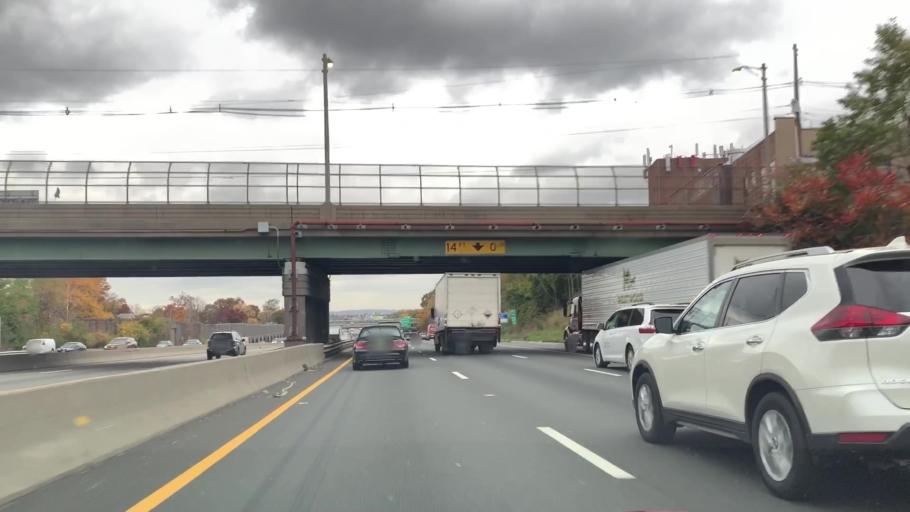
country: US
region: New Jersey
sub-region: Bergen County
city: Ridgefield Park
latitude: 40.8663
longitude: -74.0225
